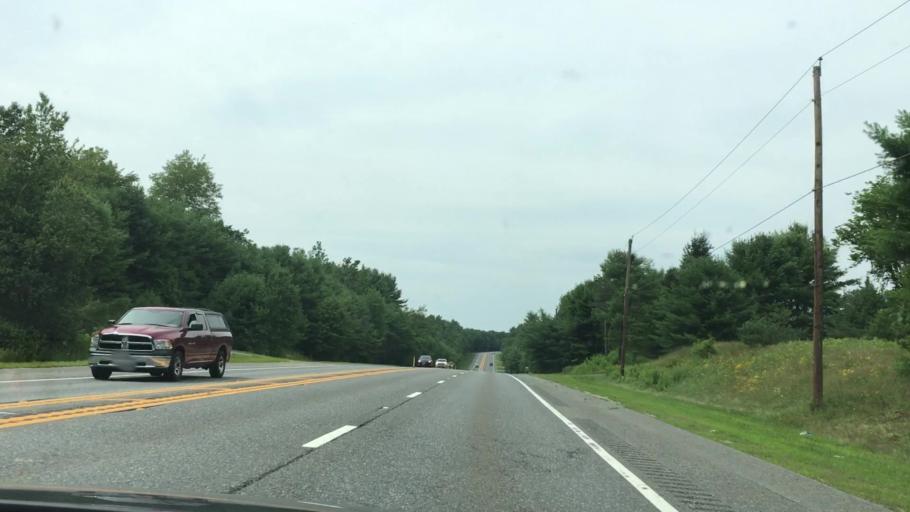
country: US
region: Massachusetts
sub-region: Worcester County
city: Gardner
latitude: 42.6119
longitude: -72.0001
